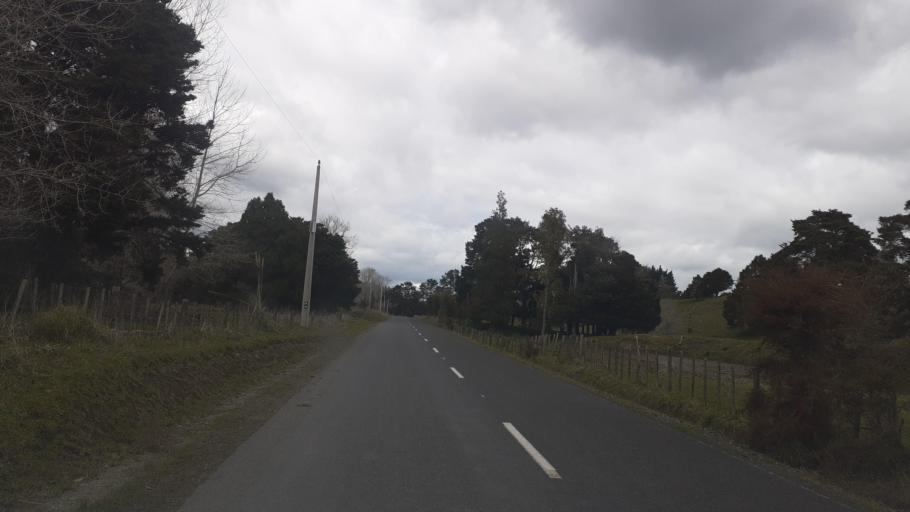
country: NZ
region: Northland
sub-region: Far North District
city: Moerewa
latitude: -35.5791
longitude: 173.9695
